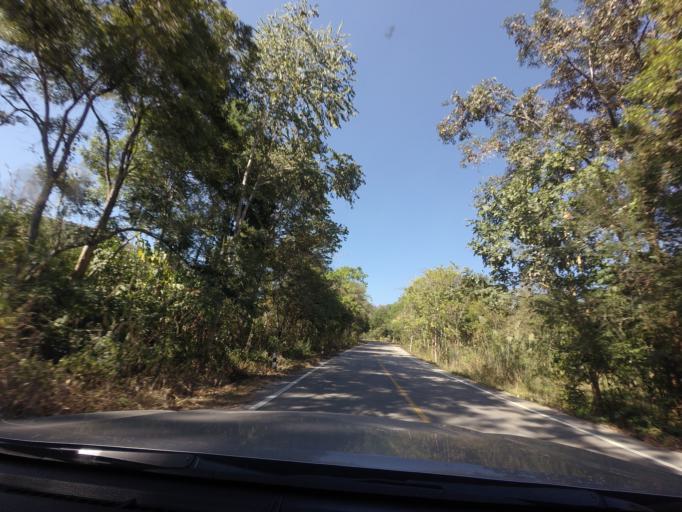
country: TH
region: Lampang
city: Chae Hom
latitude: 18.5436
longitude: 99.6381
